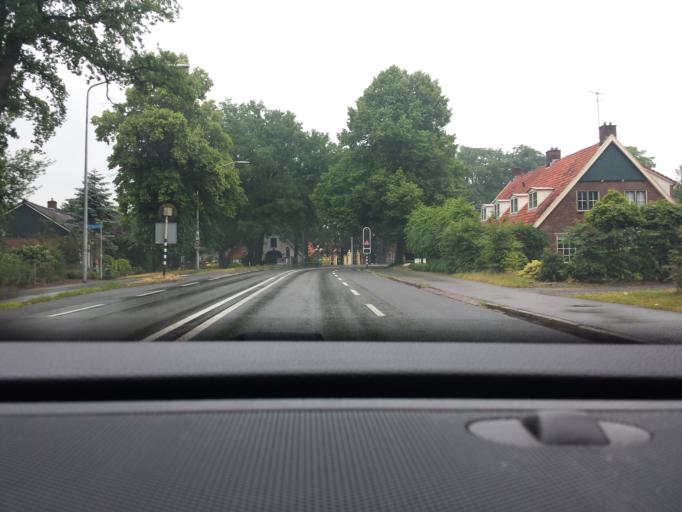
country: NL
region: Overijssel
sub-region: Gemeente Enschede
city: Enschede
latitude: 52.2021
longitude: 6.8325
